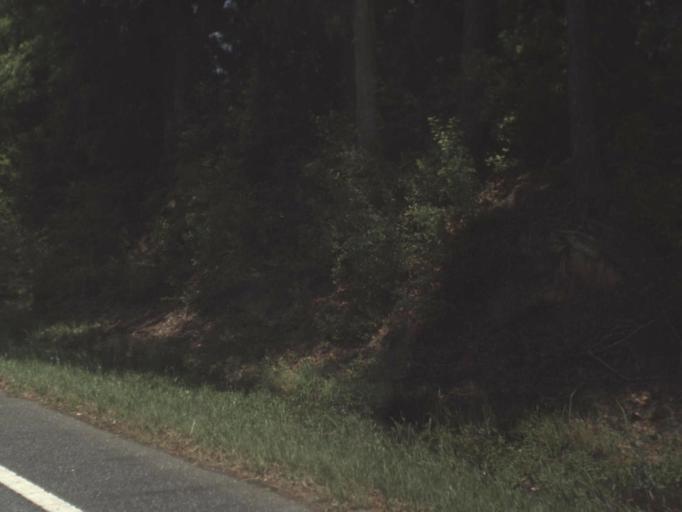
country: US
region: Florida
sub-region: Santa Rosa County
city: Point Baker
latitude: 30.8438
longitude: -87.0511
